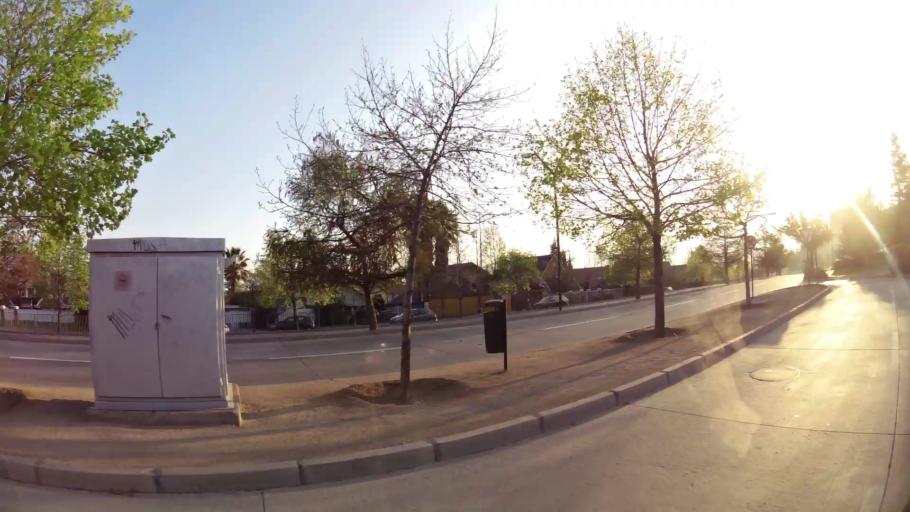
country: CL
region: Santiago Metropolitan
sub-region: Provincia de Chacabuco
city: Chicureo Abajo
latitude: -33.3263
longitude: -70.5153
